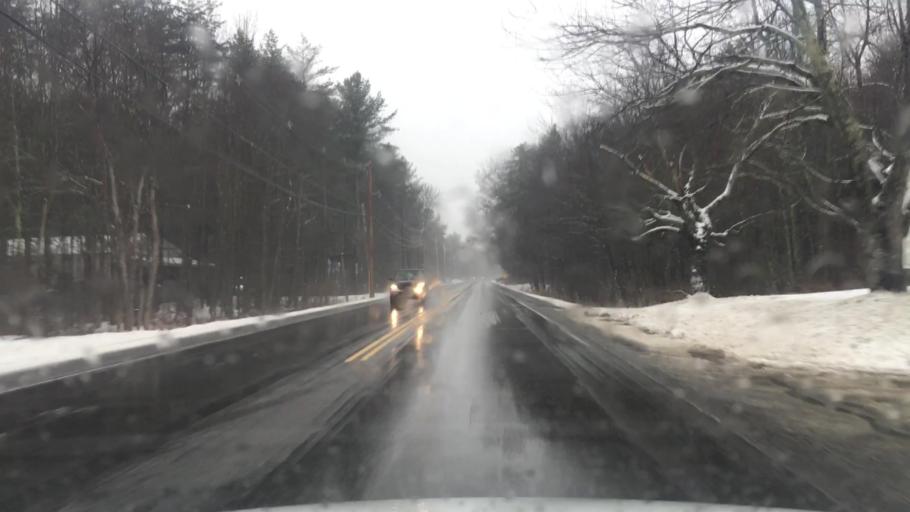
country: US
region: Maine
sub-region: York County
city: Buxton
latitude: 43.7120
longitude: -70.5151
